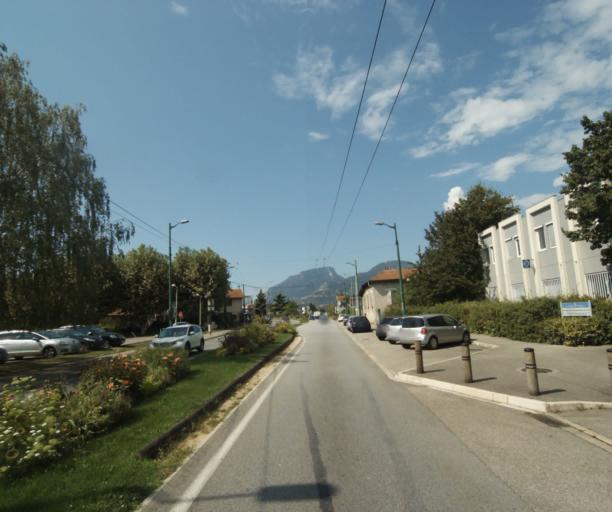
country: FR
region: Rhone-Alpes
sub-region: Departement de l'Isere
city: Eybens
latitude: 45.1606
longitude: 5.7449
